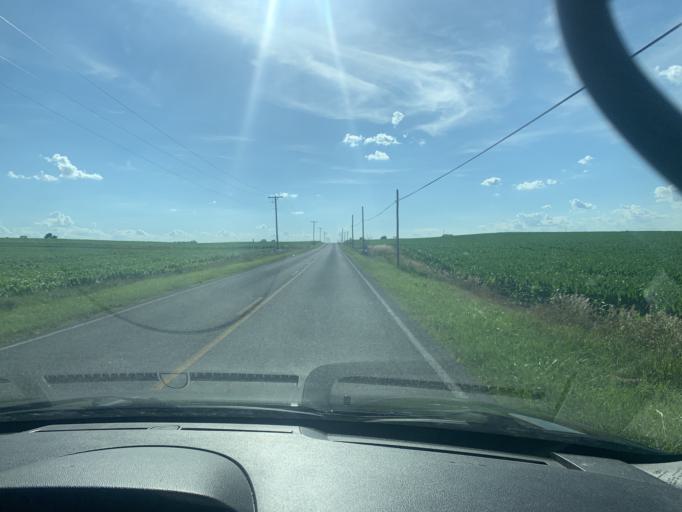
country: US
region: Ohio
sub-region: Logan County
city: Bellefontaine
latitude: 40.3433
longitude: -83.8244
